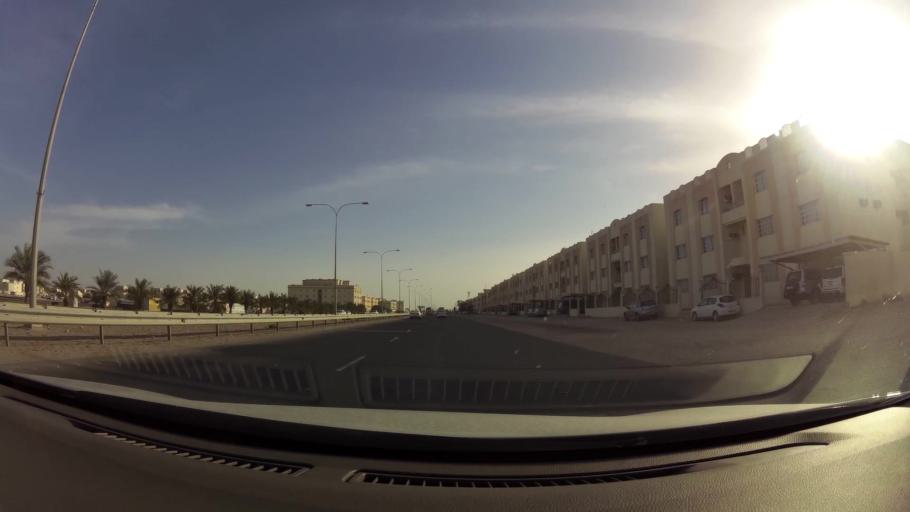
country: QA
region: Al Wakrah
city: Al Wakrah
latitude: 25.1552
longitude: 51.6044
